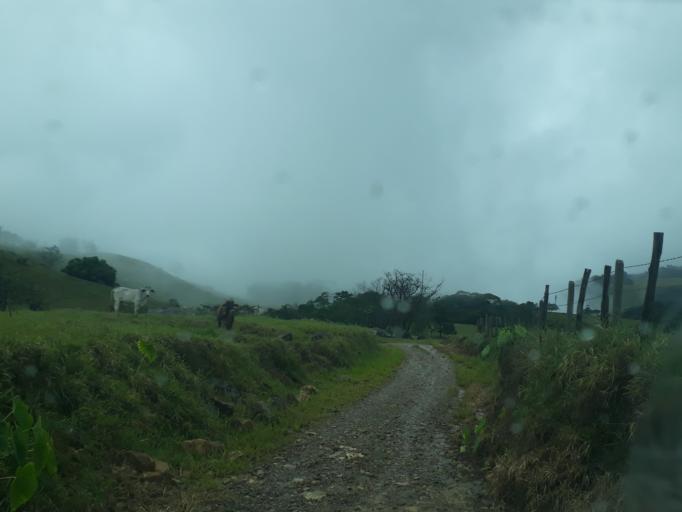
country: CO
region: Cundinamarca
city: Medina
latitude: 4.5351
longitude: -73.3833
